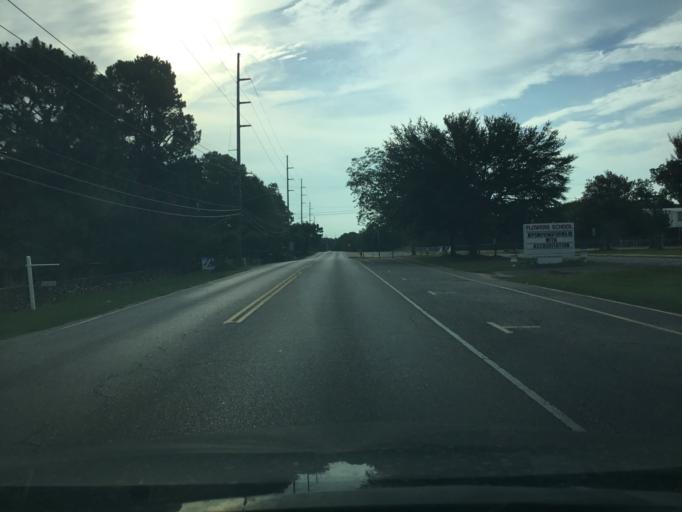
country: US
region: Alabama
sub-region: Montgomery County
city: Montgomery
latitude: 32.3670
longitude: -86.2523
